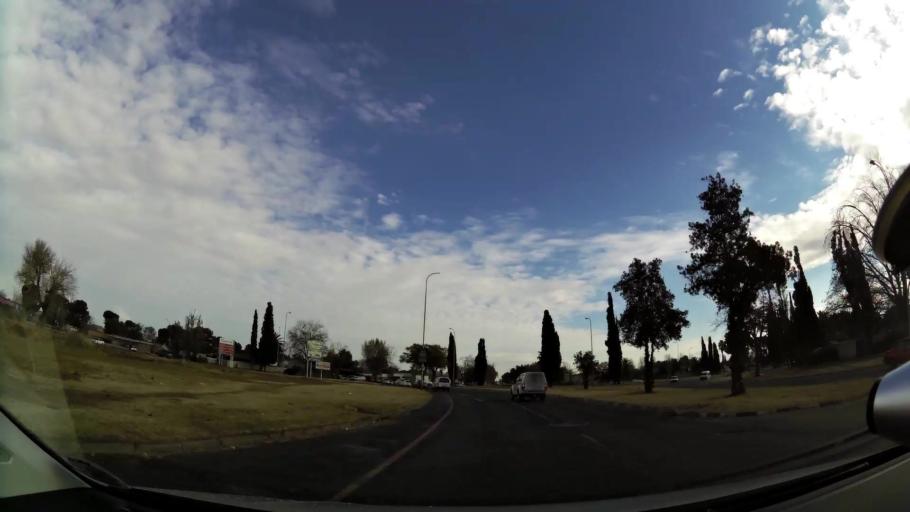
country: ZA
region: Orange Free State
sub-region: Lejweleputswa District Municipality
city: Welkom
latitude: -27.9866
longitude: 26.7567
